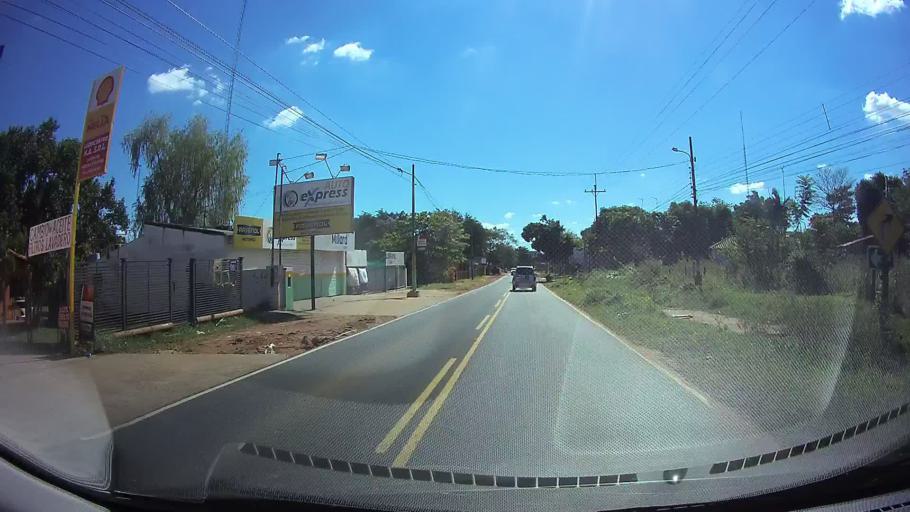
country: PY
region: Central
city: Limpio
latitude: -25.2038
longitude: -57.4634
